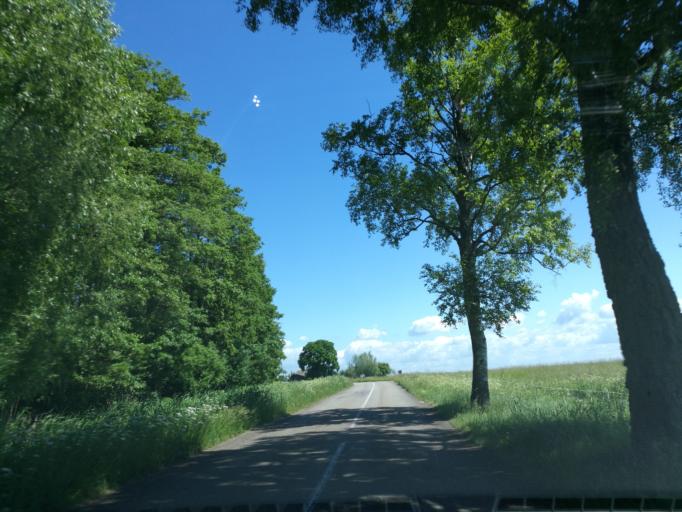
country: LT
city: Rusne
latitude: 55.3856
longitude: 21.2396
